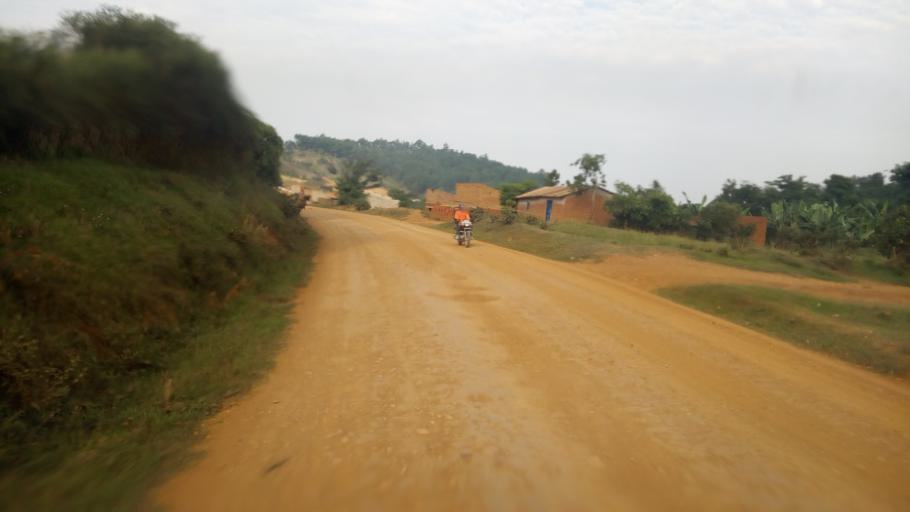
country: UG
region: Western Region
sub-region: Kanungu District
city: Ntungamo
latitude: -0.8284
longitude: 29.6997
